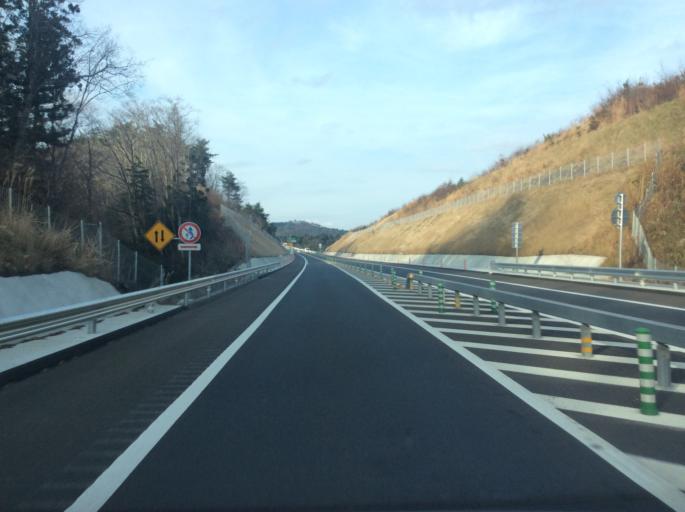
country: JP
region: Fukushima
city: Namie
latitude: 37.4196
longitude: 140.9625
